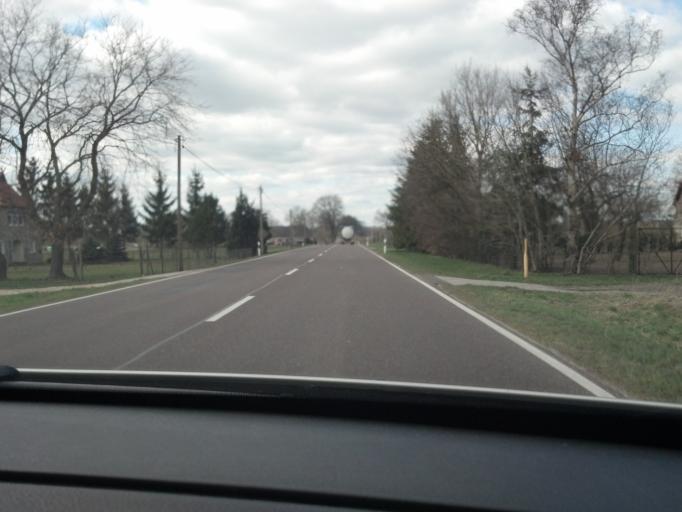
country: DE
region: Mecklenburg-Vorpommern
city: Robel
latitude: 53.3393
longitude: 12.5360
